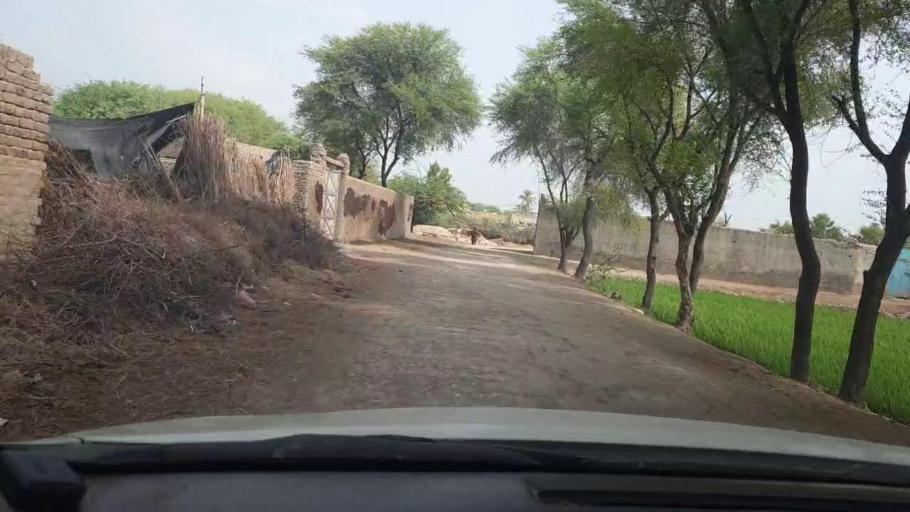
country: PK
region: Sindh
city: Shikarpur
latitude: 28.0041
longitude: 68.5930
